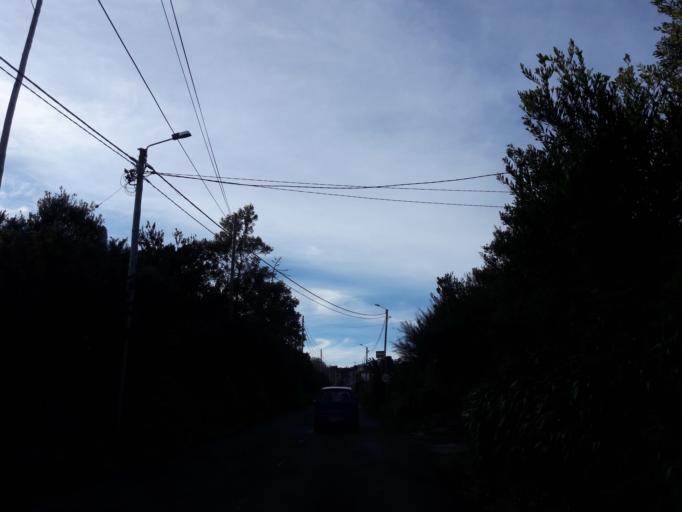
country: PT
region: Madeira
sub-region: Santa Cruz
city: Camacha
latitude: 32.6671
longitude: -16.8412
